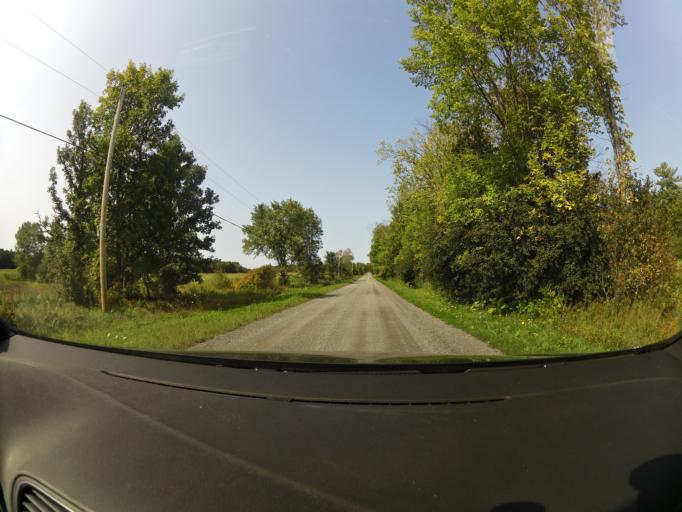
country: CA
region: Ontario
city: Arnprior
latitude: 45.4473
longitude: -76.1652
